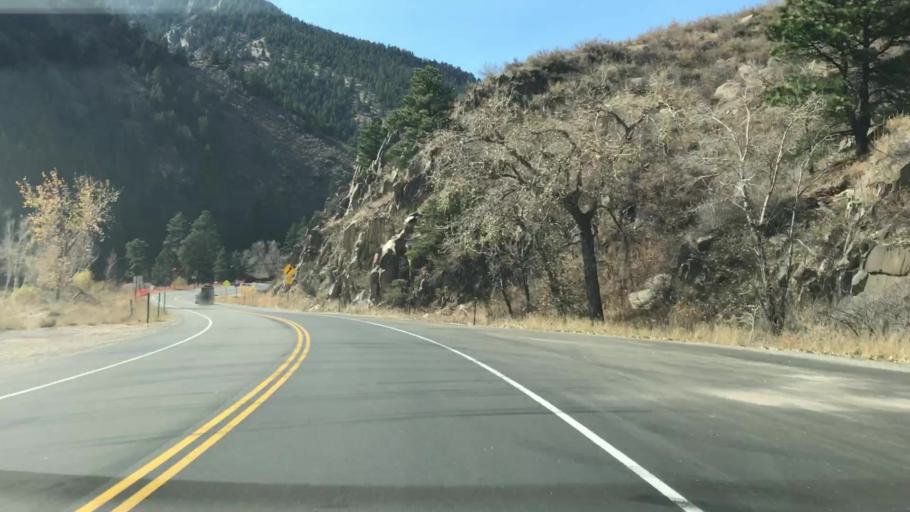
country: US
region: Colorado
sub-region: Boulder County
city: Lyons
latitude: 40.4298
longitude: -105.3163
